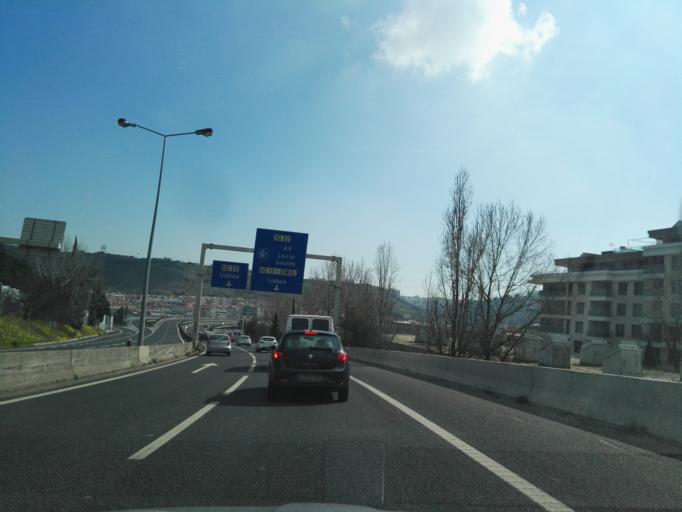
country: PT
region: Lisbon
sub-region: Odivelas
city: Olival do Basto
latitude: 38.7936
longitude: -9.1729
